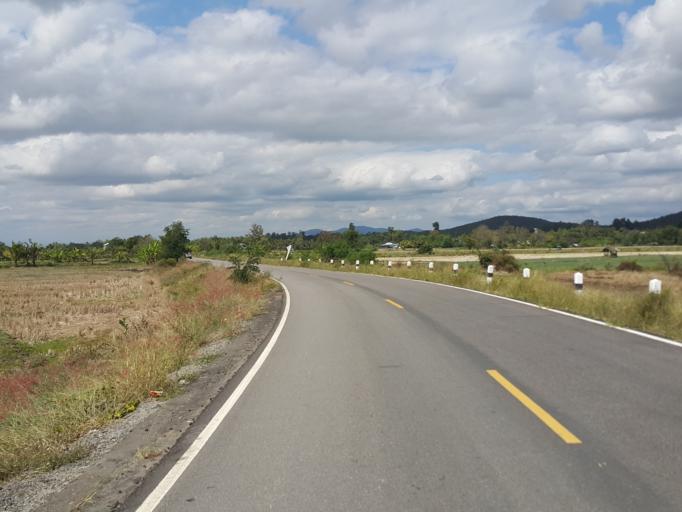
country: TH
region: Chiang Mai
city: Mae On
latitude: 18.8245
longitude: 99.1720
